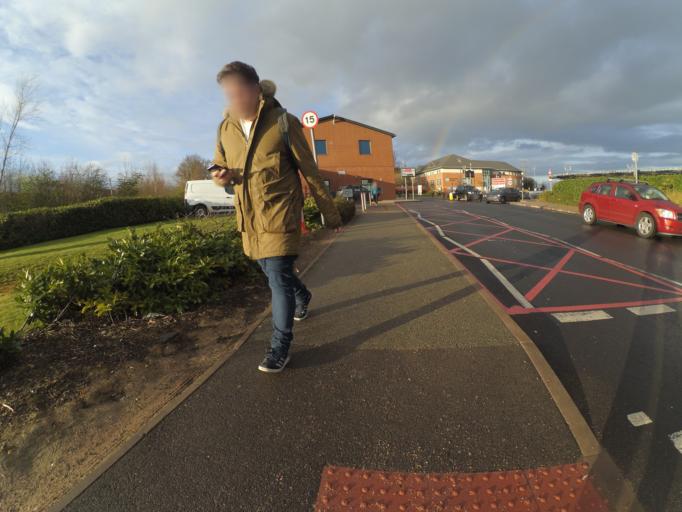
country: GB
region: England
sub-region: Warwickshire
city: Brandon
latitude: 52.4223
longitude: -1.4398
